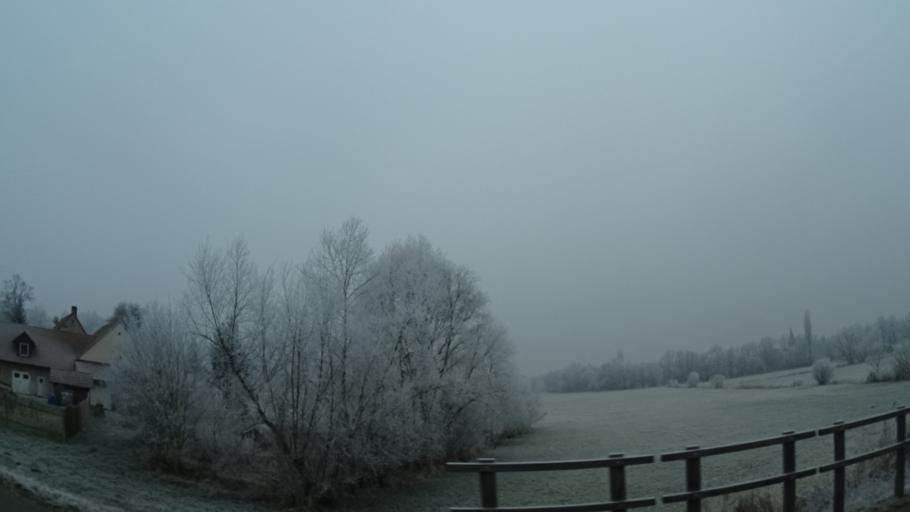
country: DE
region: Bavaria
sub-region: Regierungsbezirk Unterfranken
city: Hassfurt
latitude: 50.0529
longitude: 10.5268
